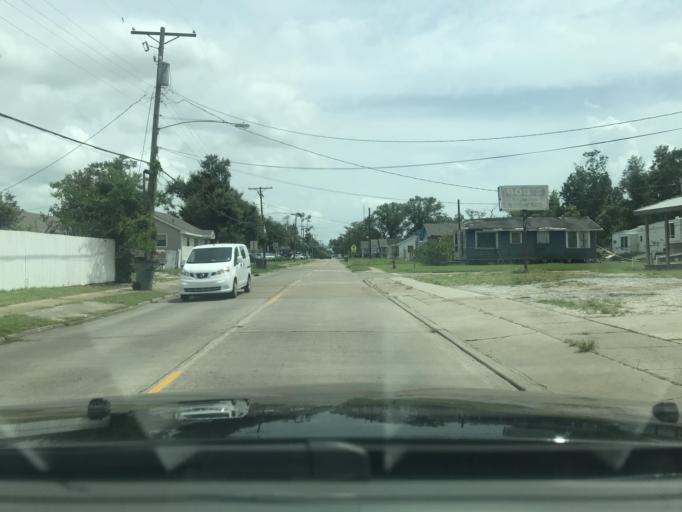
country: US
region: Louisiana
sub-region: Calcasieu Parish
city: Lake Charles
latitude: 30.2058
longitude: -93.2141
